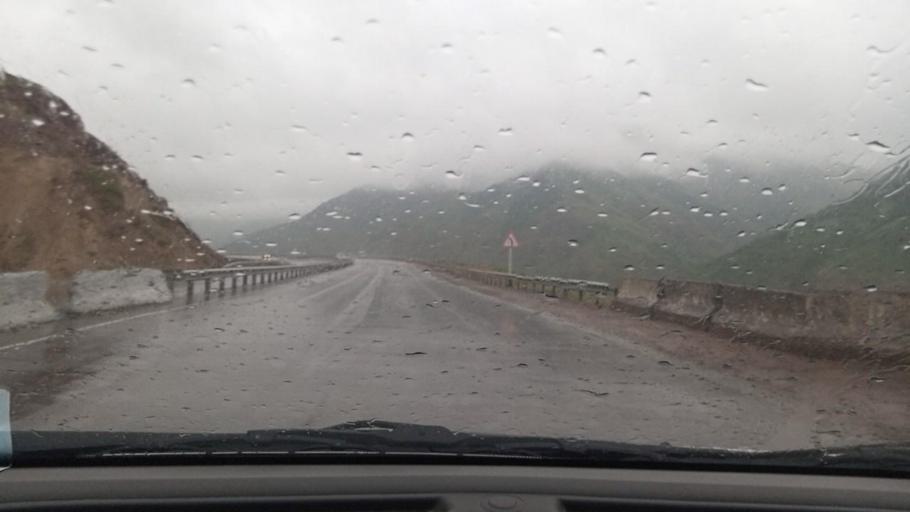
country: UZ
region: Toshkent
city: Angren
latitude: 41.0721
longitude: 70.2724
